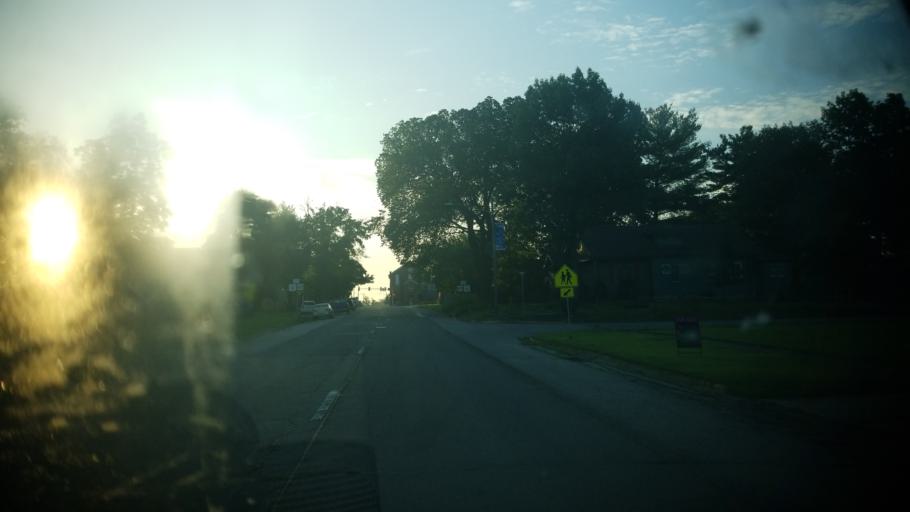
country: US
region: Illinois
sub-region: Wayne County
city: Fairfield
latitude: 38.3788
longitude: -88.3625
